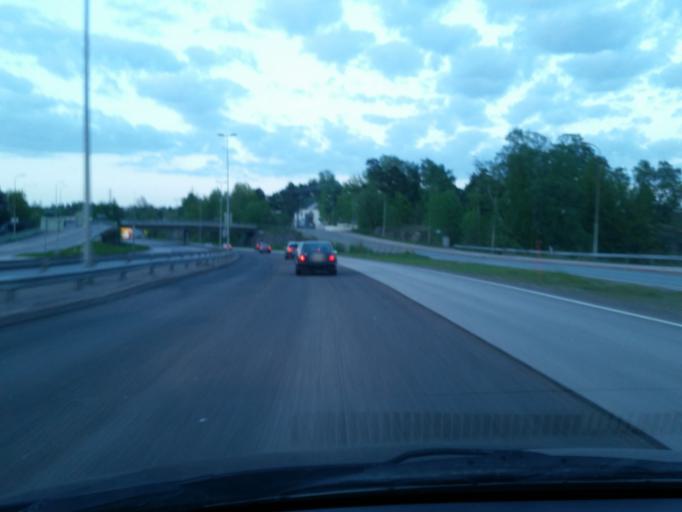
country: FI
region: Uusimaa
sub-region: Helsinki
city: Helsinki
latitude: 60.1857
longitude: 24.9906
